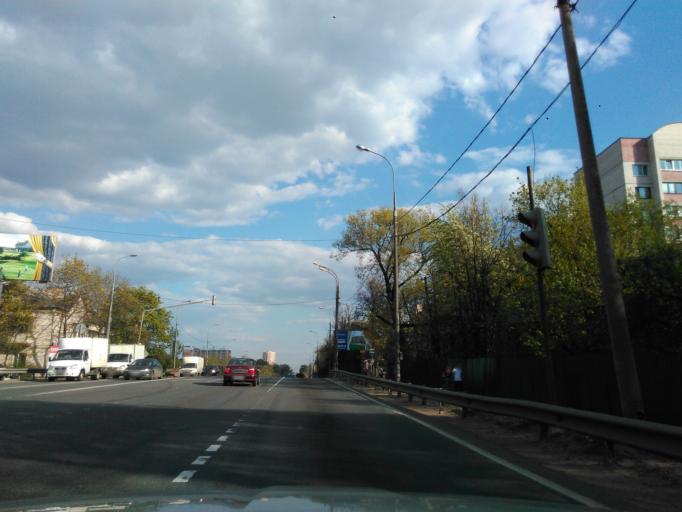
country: RU
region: Moskovskaya
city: Solnechnogorsk
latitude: 56.1951
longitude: 36.9654
